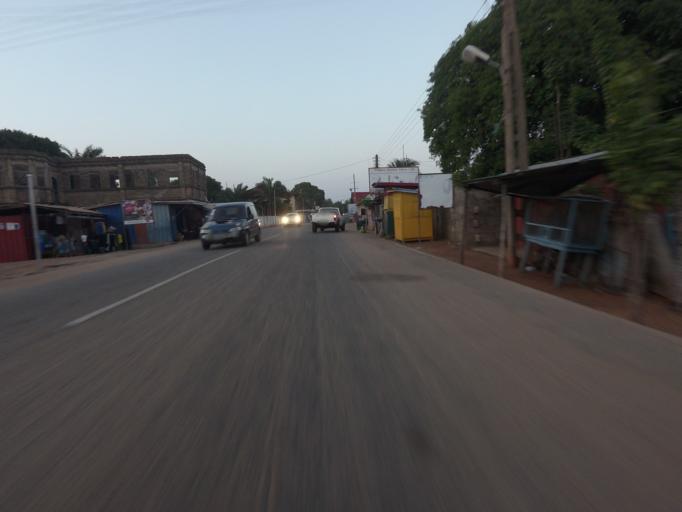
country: GH
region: Volta
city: Keta
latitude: 5.8931
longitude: 0.9858
